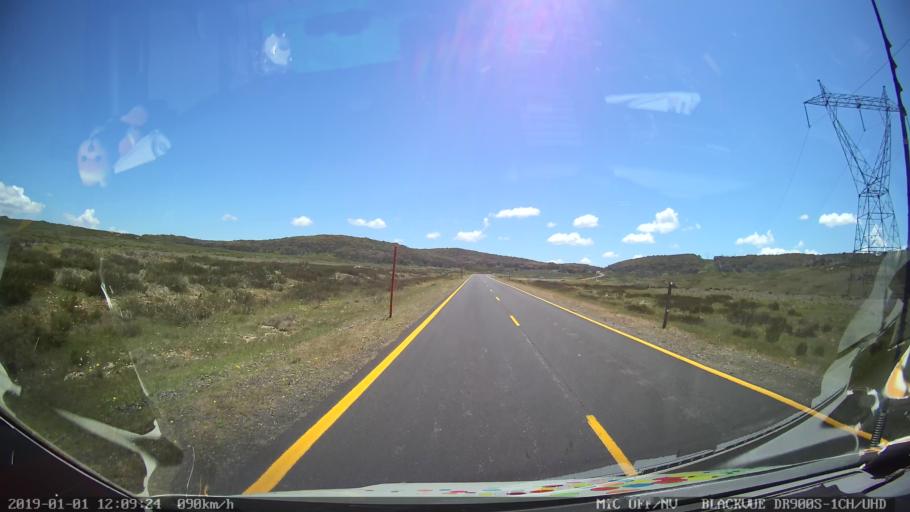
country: AU
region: New South Wales
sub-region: Tumut Shire
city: Tumut
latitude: -35.8077
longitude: 148.4961
